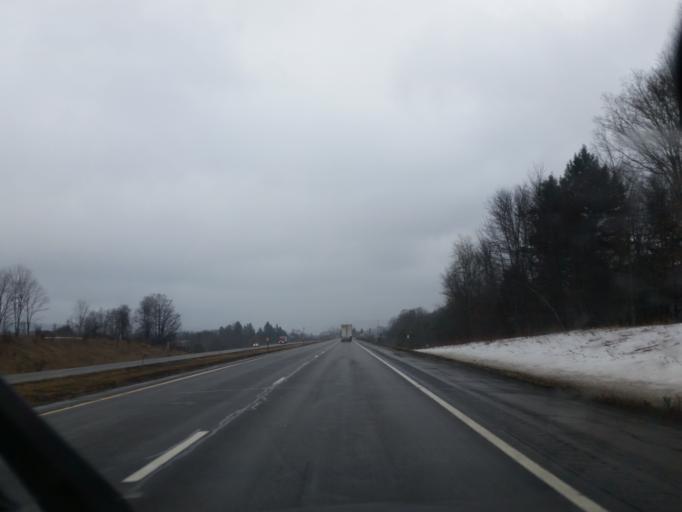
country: US
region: New York
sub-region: Chenango County
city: Lakeview
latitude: 42.3171
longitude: -75.9619
